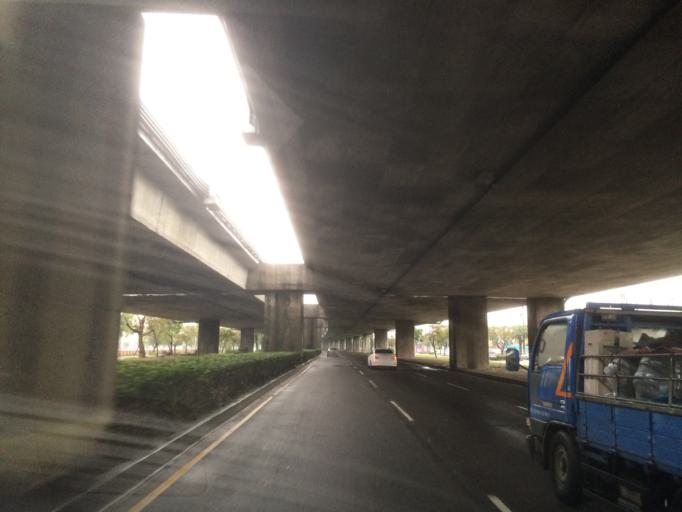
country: TW
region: Taiwan
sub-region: Taichung City
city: Taichung
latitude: 24.1590
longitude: 120.6266
